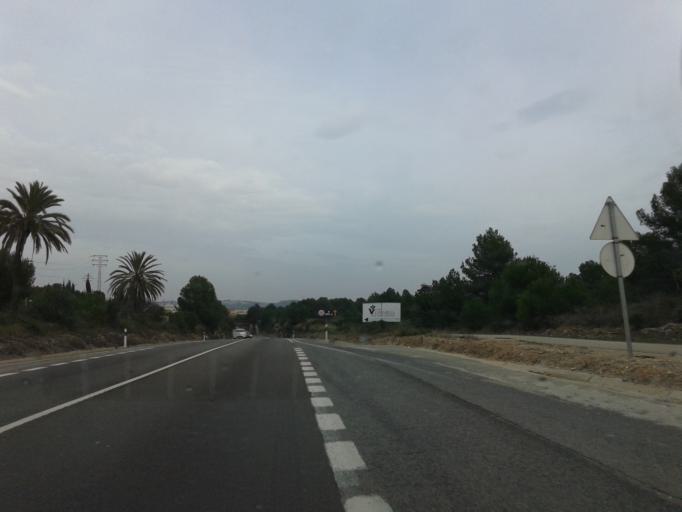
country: ES
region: Catalonia
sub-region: Provincia de Tarragona
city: Roda de Bara
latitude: 41.1824
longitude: 1.5077
